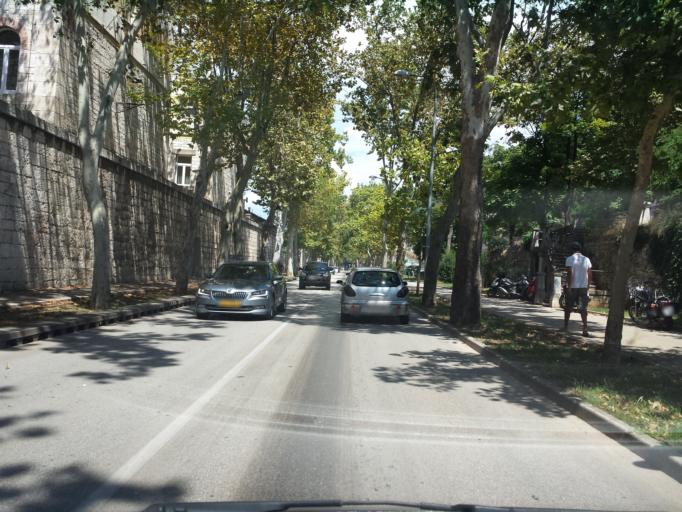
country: HR
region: Istarska
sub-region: Grad Pula
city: Pula
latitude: 44.8637
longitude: 13.8412
